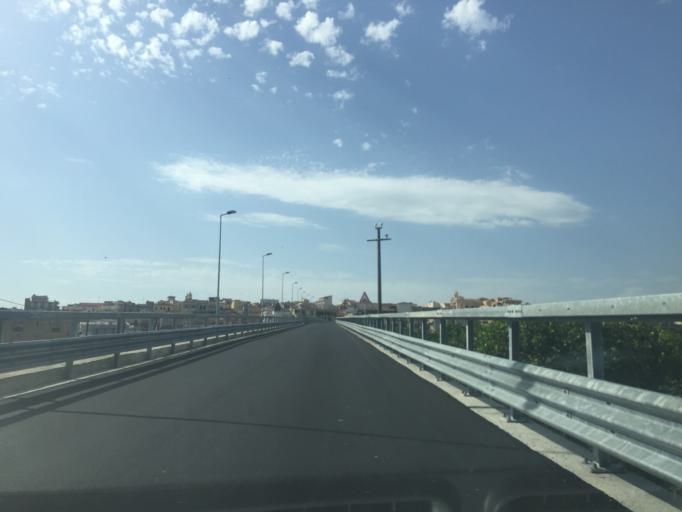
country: IT
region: Sicily
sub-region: Provincia di Siracusa
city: Rosolini
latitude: 36.8160
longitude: 14.9555
